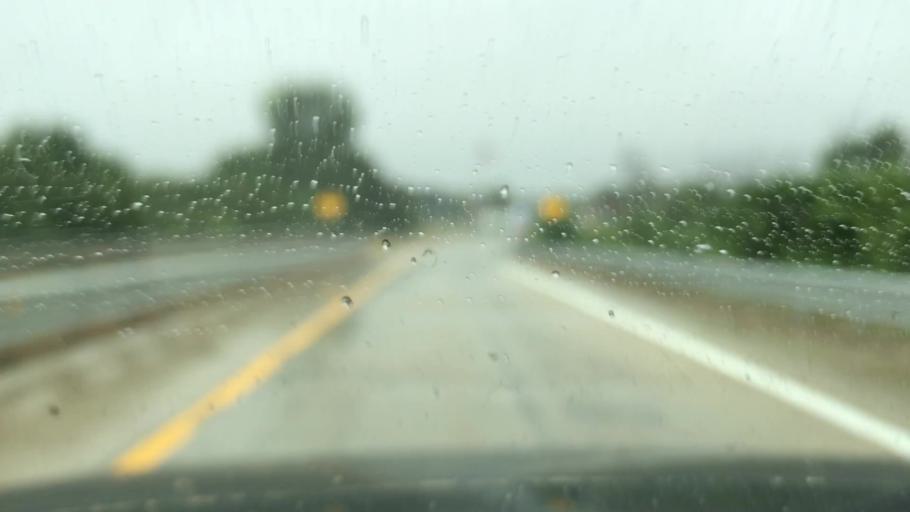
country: US
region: Michigan
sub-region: Kent County
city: Grandville
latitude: 42.9157
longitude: -85.7626
